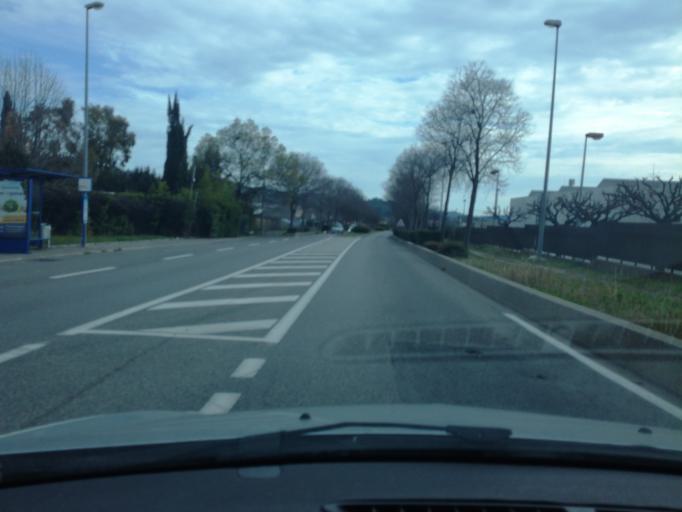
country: FR
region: Provence-Alpes-Cote d'Azur
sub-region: Departement des Alpes-Maritimes
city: Mouans-Sartoux
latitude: 43.6499
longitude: 6.9496
